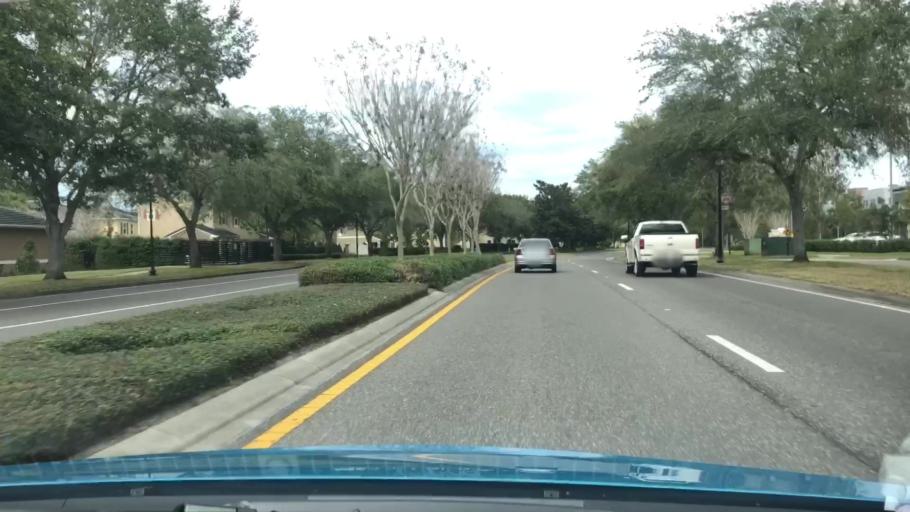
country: US
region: Florida
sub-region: Seminole County
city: Heathrow
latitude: 28.7811
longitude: -81.3577
